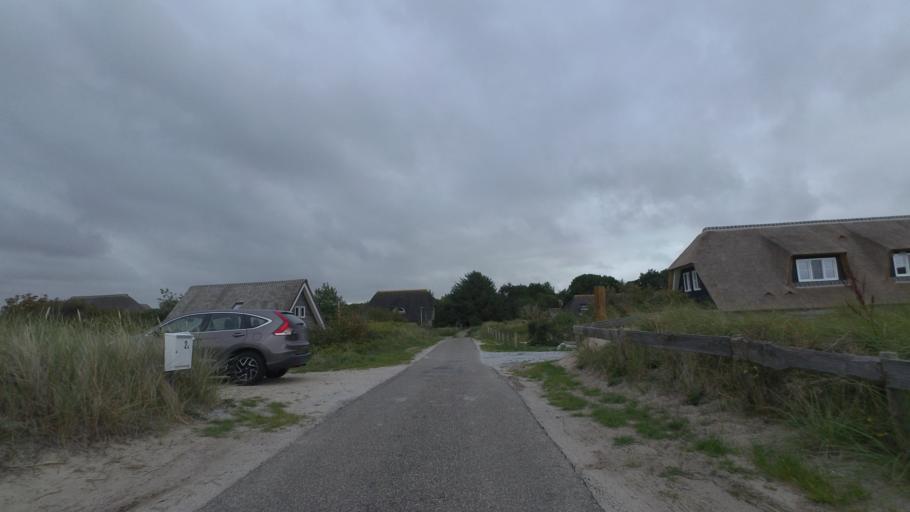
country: NL
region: Friesland
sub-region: Gemeente Ameland
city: Nes
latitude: 53.4566
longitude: 5.7889
